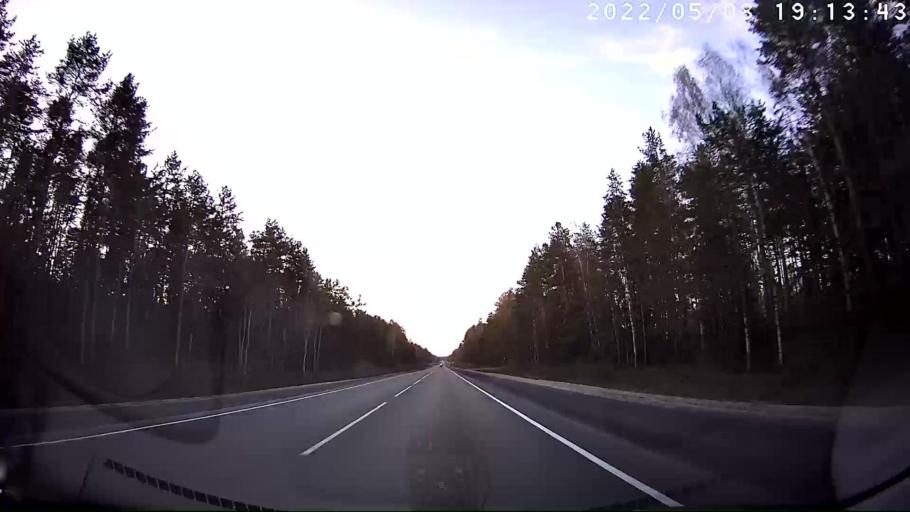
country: RU
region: Mariy-El
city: Suslonger
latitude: 56.3049
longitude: 48.2346
